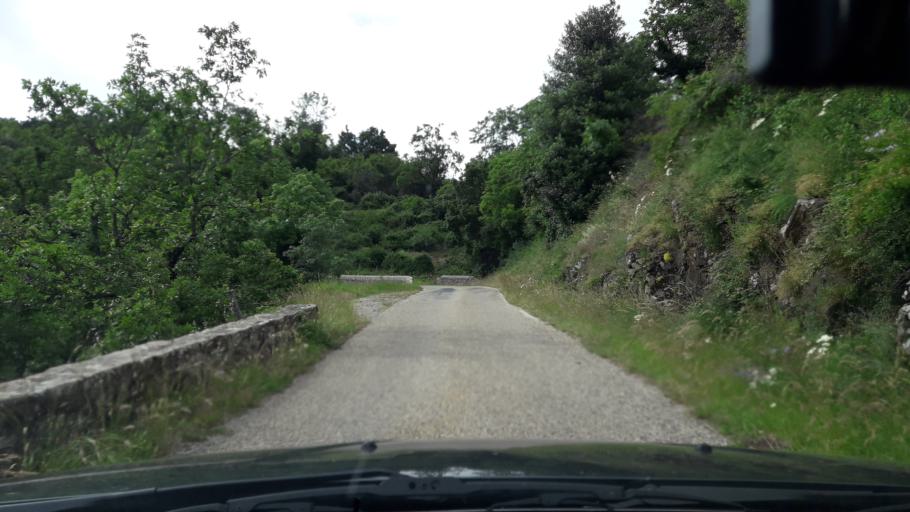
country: FR
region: Rhone-Alpes
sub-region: Departement de l'Ardeche
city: Saint-Priest
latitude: 44.6817
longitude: 4.5759
